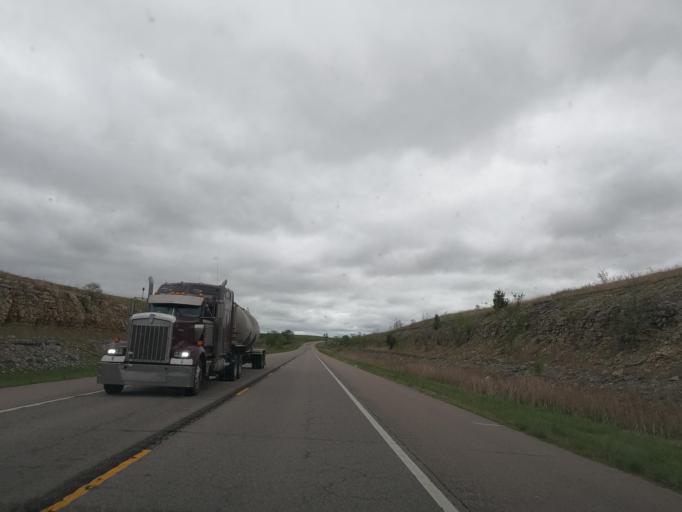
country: US
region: Kansas
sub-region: Greenwood County
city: Eureka
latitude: 37.6546
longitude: -96.4684
